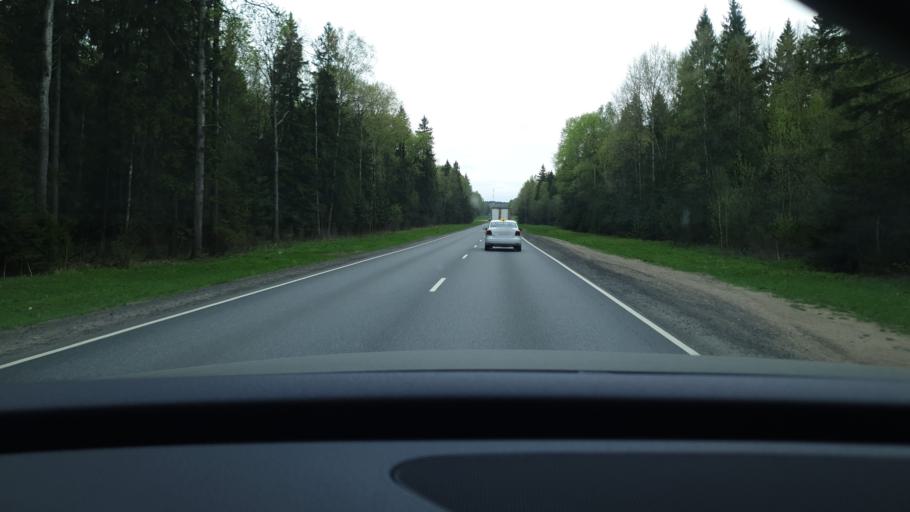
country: RU
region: Moskovskaya
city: Novopetrovskoye
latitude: 56.0483
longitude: 36.5003
